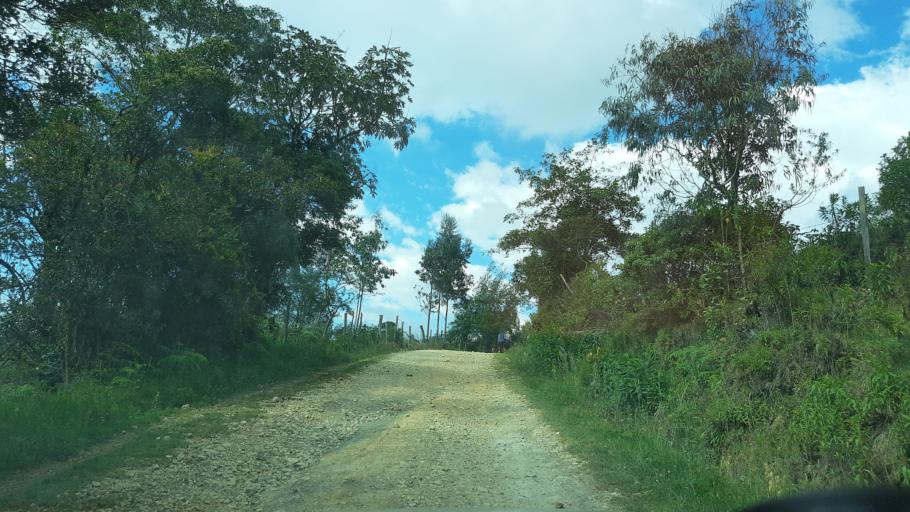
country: CO
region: Boyaca
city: Santa Sofia
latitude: 5.7355
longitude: -73.5520
